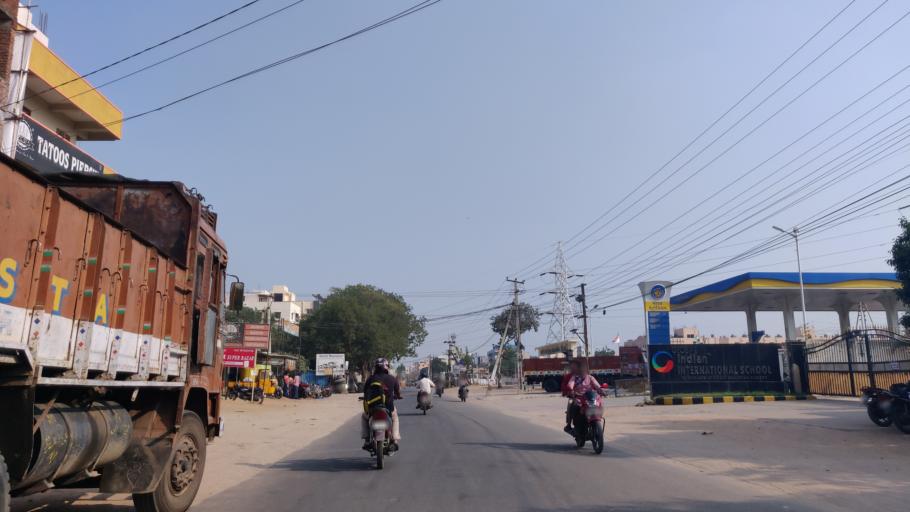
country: IN
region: Telangana
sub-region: Rangareddi
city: Uppal Kalan
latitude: 17.3973
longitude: 78.5883
